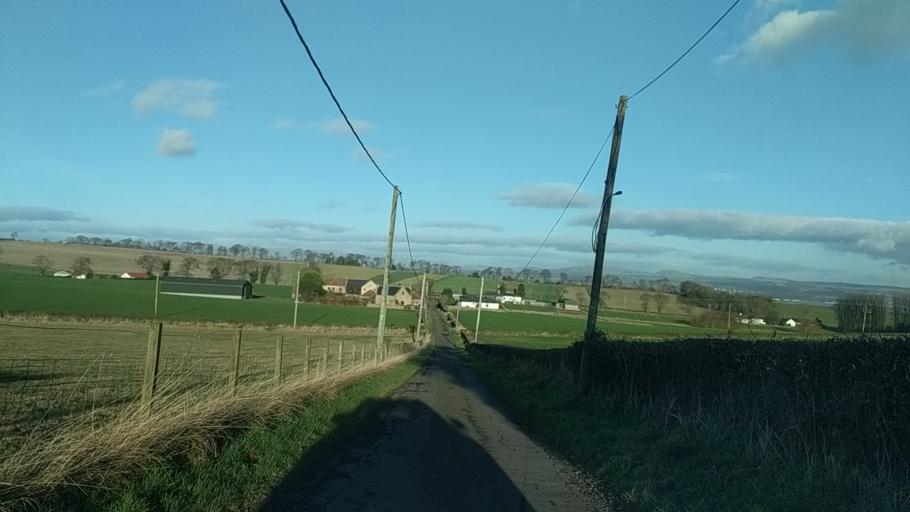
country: GB
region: Scotland
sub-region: West Lothian
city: Linlithgow
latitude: 55.9938
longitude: -3.5432
